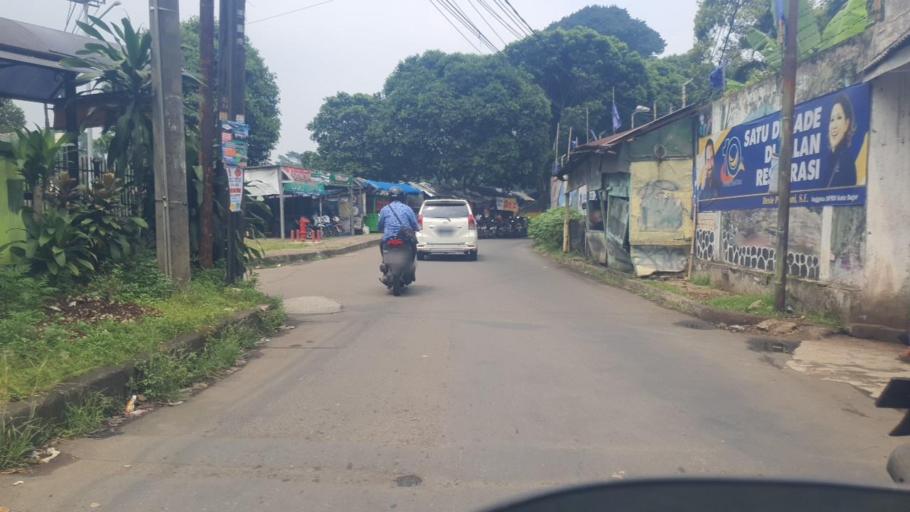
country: ID
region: West Java
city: Bogor
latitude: -6.5832
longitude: 106.7864
